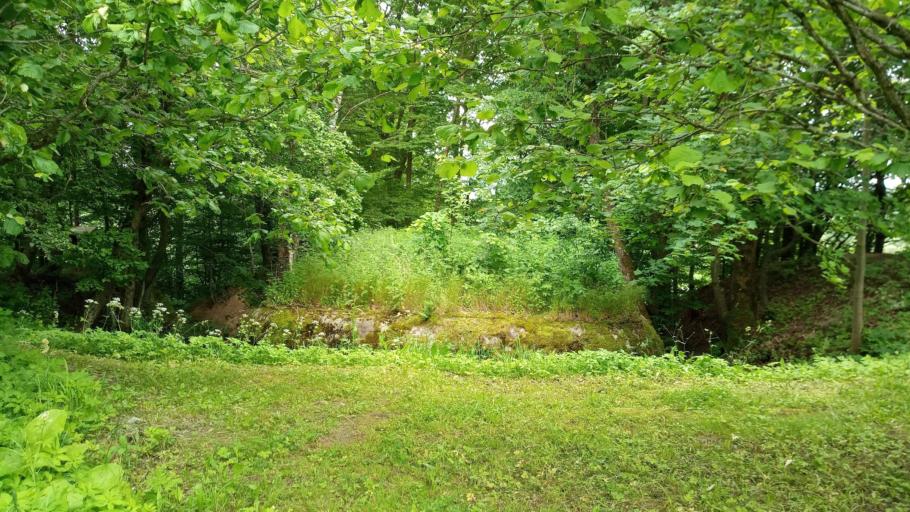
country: LT
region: Taurages apskritis
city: Taurage
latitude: 55.3554
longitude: 22.2201
